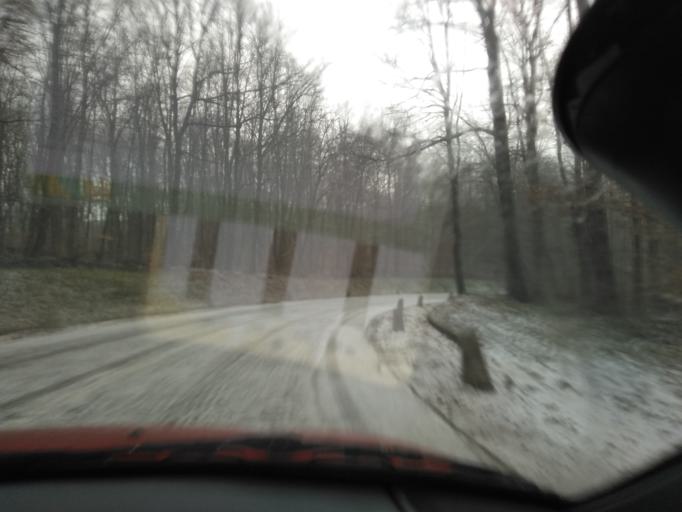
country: AT
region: Lower Austria
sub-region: Politischer Bezirk Wien-Umgebung
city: Klosterneuburg
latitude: 48.2603
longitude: 16.2887
